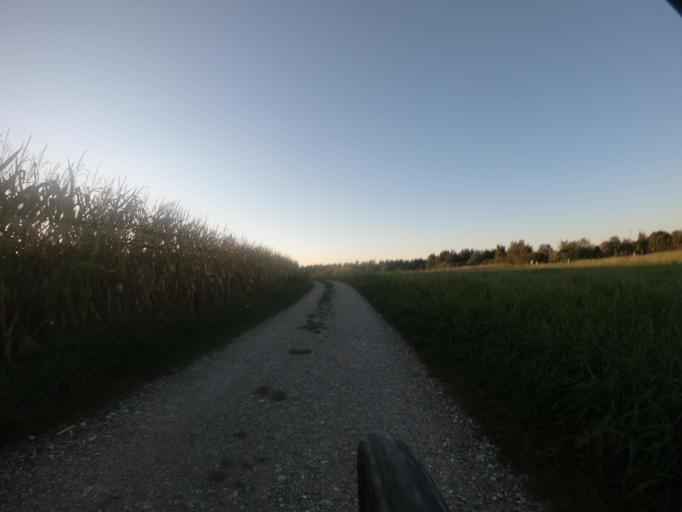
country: DE
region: Bavaria
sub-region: Upper Bavaria
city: Emmering
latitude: 48.1889
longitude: 11.2708
